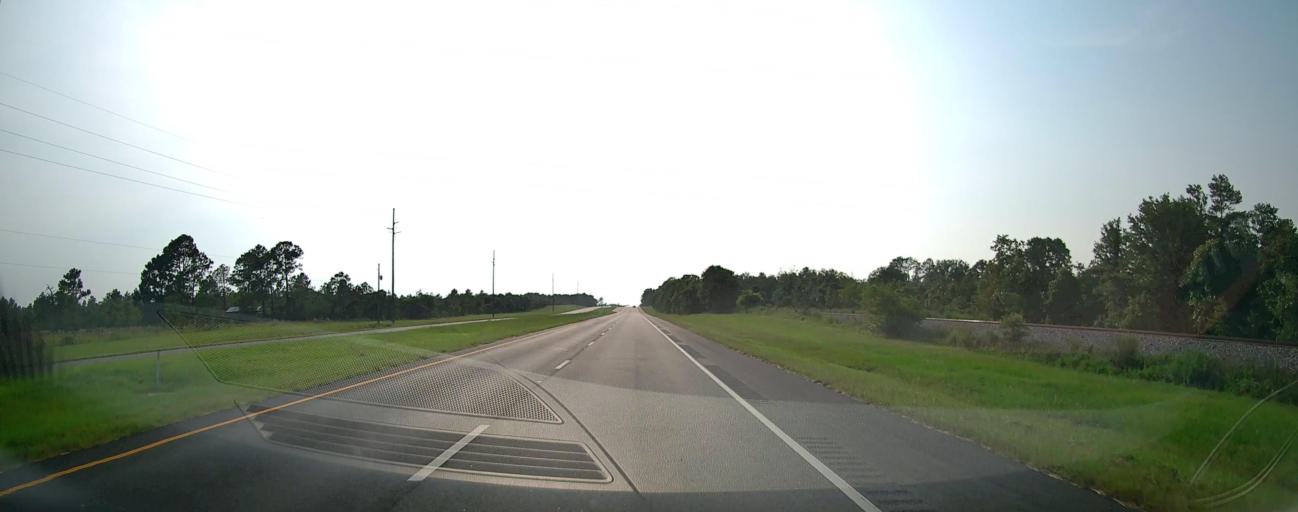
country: US
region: Georgia
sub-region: Taylor County
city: Butler
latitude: 32.5850
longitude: -84.3395
